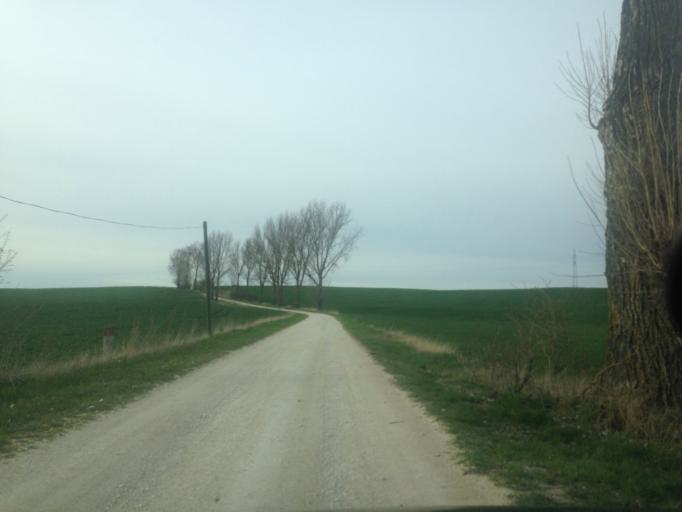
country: PL
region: Kujawsko-Pomorskie
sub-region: Powiat grudziadzki
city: Swiecie nad Osa
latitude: 53.4874
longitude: 19.1559
